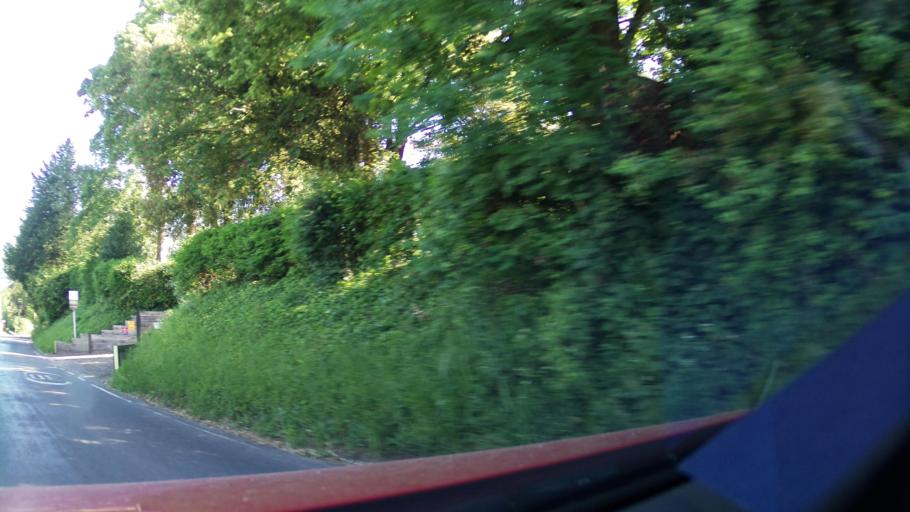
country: GB
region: England
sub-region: Hampshire
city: Winchester
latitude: 51.0895
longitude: -1.3512
